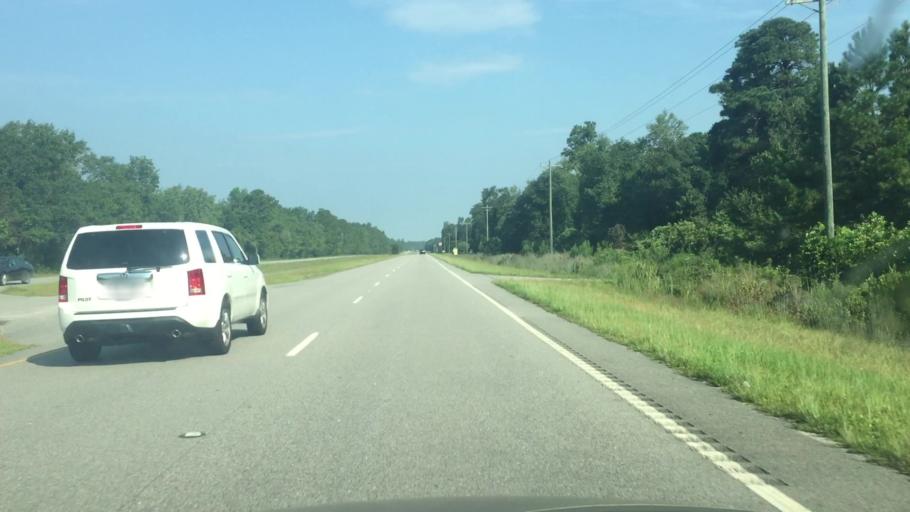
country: US
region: South Carolina
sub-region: Horry County
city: Loris
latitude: 34.0520
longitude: -78.8386
